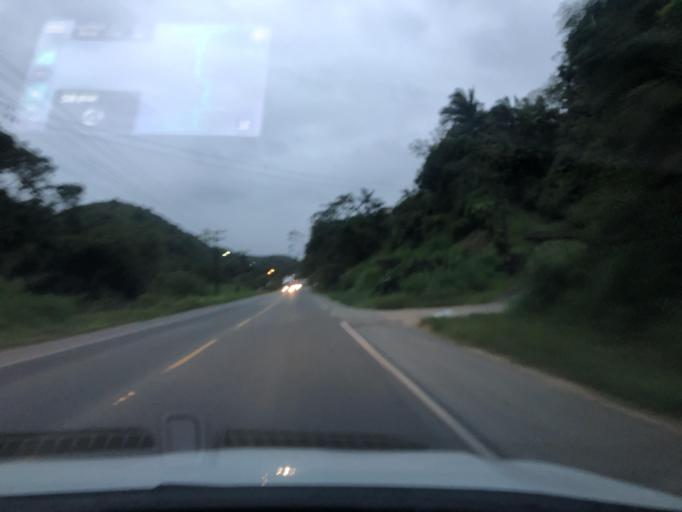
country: BR
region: Santa Catarina
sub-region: Pomerode
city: Pomerode
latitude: -26.7050
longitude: -49.0535
